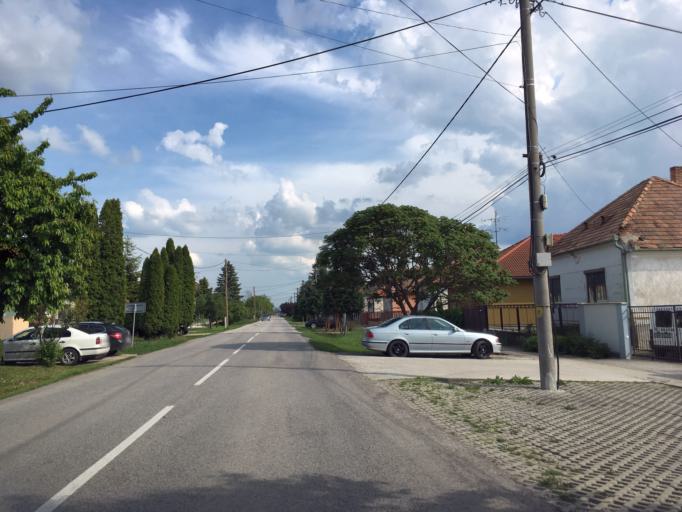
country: SK
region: Nitriansky
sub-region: Okres Komarno
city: Hurbanovo
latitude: 47.8108
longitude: 18.2247
